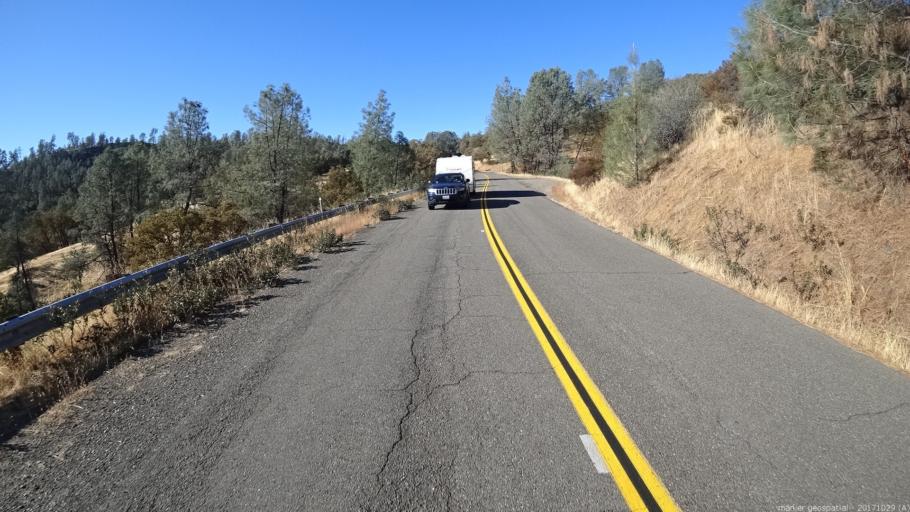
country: US
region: California
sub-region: Trinity County
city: Lewiston
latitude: 40.3997
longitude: -122.7809
